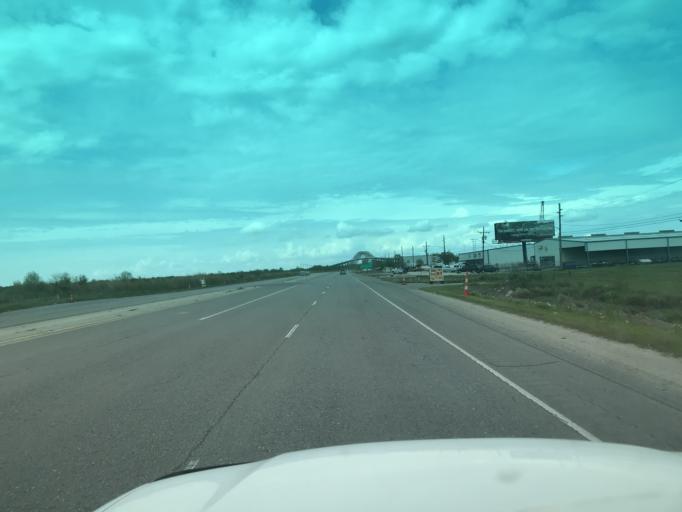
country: US
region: Louisiana
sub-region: Saint Bernard Parish
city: Chalmette
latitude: 29.9849
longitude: -89.9445
